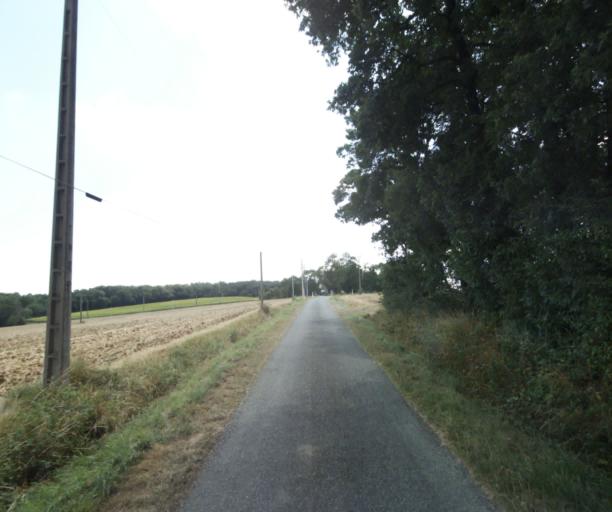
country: FR
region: Midi-Pyrenees
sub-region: Departement de la Haute-Garonne
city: Auriac-sur-Vendinelle
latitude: 43.4593
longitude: 1.8039
